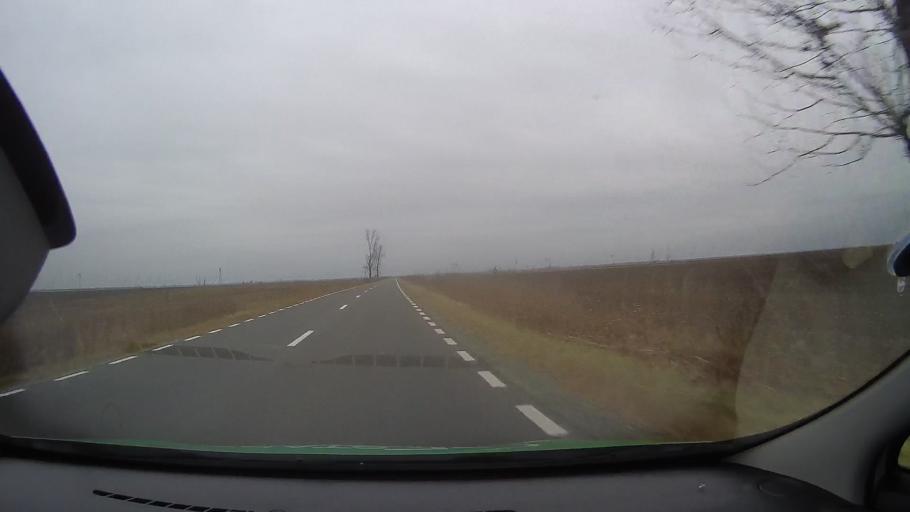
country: RO
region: Ialomita
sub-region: Comuna Gheorghe Lazar
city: Gheorghe Lazar
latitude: 44.6579
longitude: 27.4117
